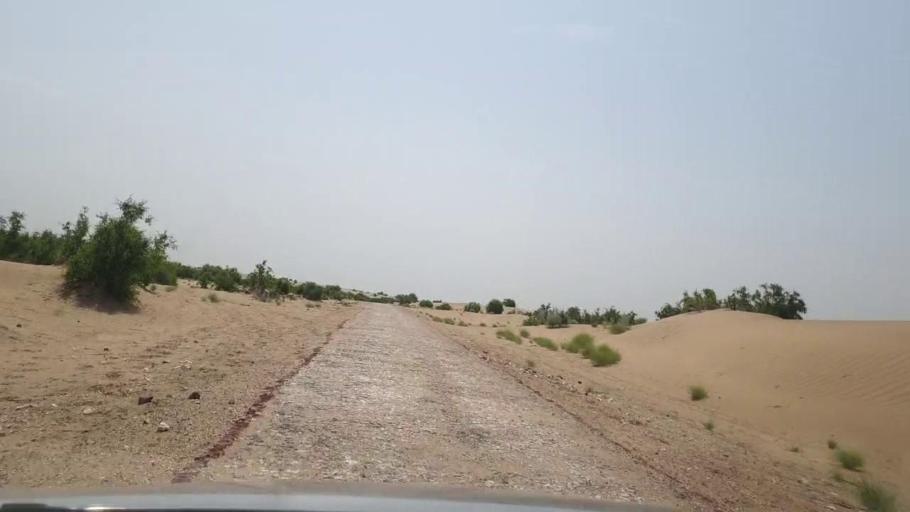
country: PK
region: Sindh
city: Pano Aqil
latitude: 27.5812
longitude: 69.1735
